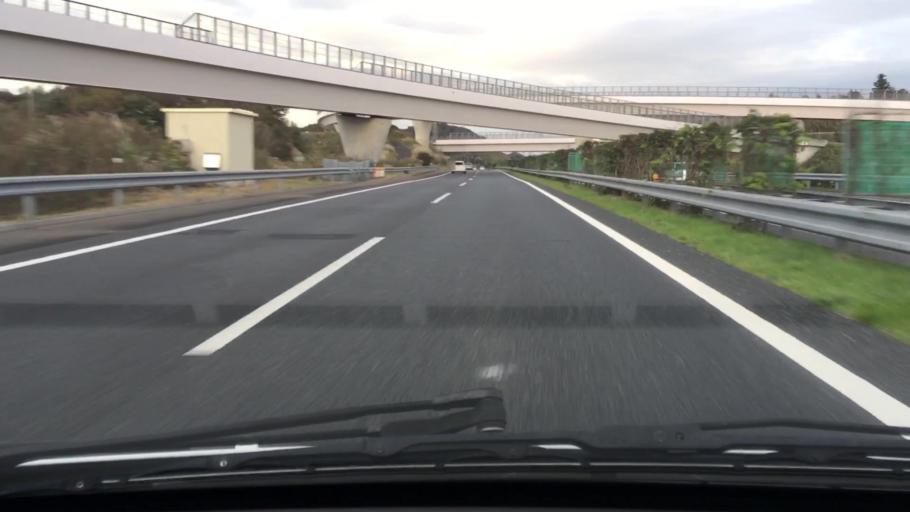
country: JP
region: Chiba
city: Kisarazu
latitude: 35.3748
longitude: 139.9778
